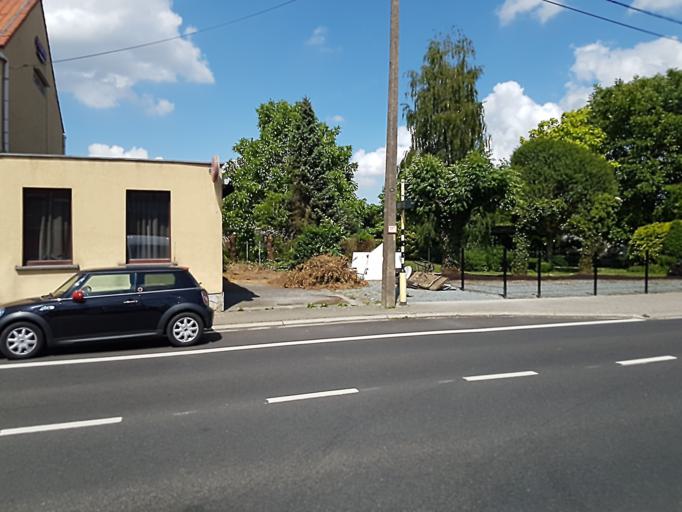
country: BE
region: Flanders
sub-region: Provincie Vlaams-Brabant
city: Overijse
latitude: 50.7770
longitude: 4.5273
